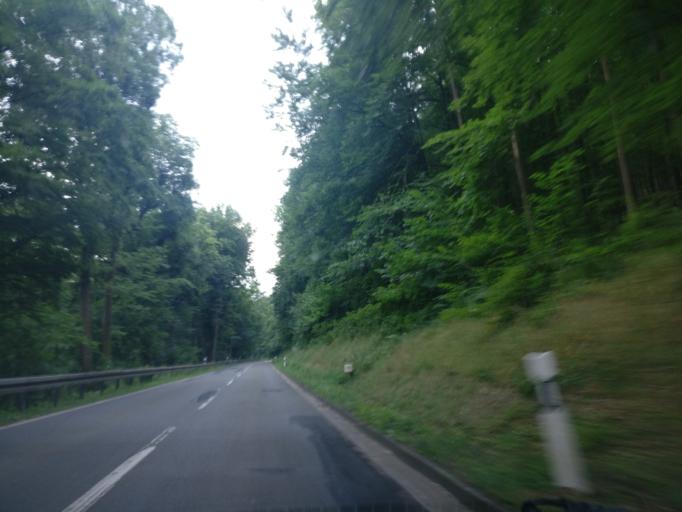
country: DE
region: Lower Saxony
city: Bodenfelde
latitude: 51.6260
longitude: 9.5946
